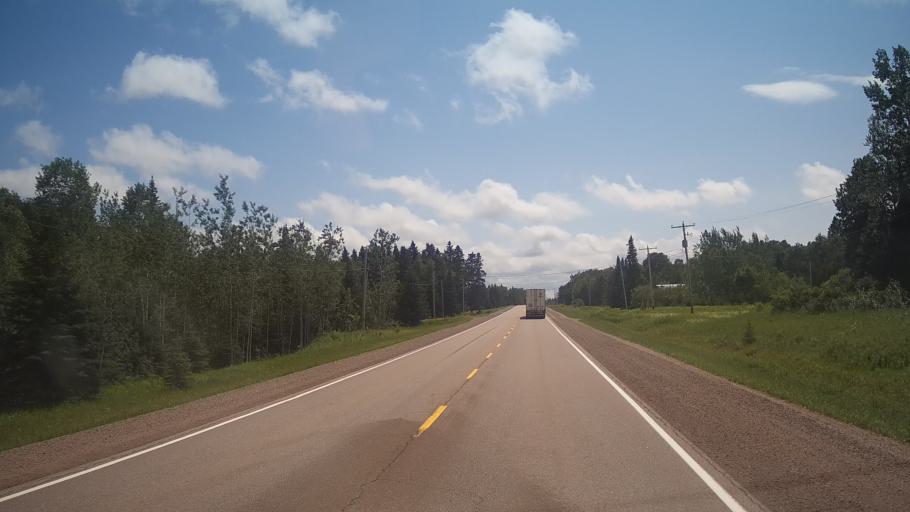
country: CA
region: Ontario
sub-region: Thunder Bay District
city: Thunder Bay
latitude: 48.8321
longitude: -88.5262
